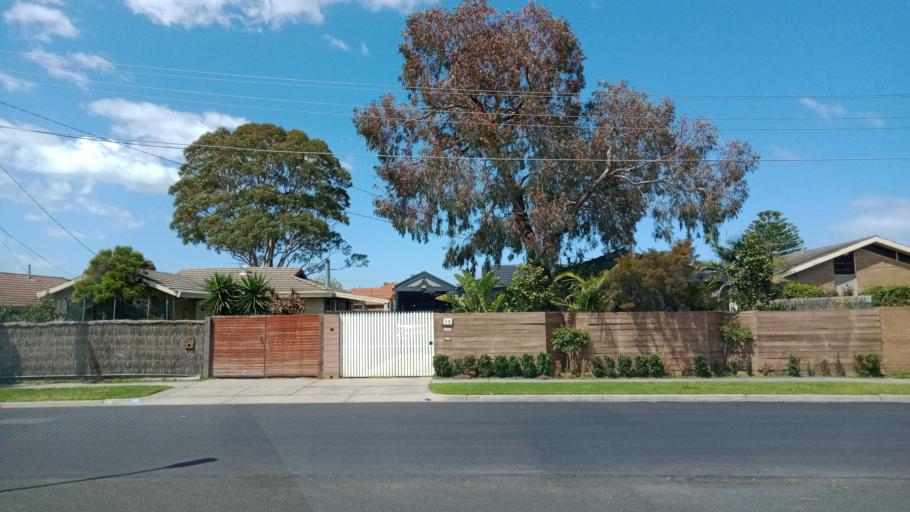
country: AU
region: Victoria
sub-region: Kingston
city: Chelsea Heights
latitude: -38.0481
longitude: 145.1377
